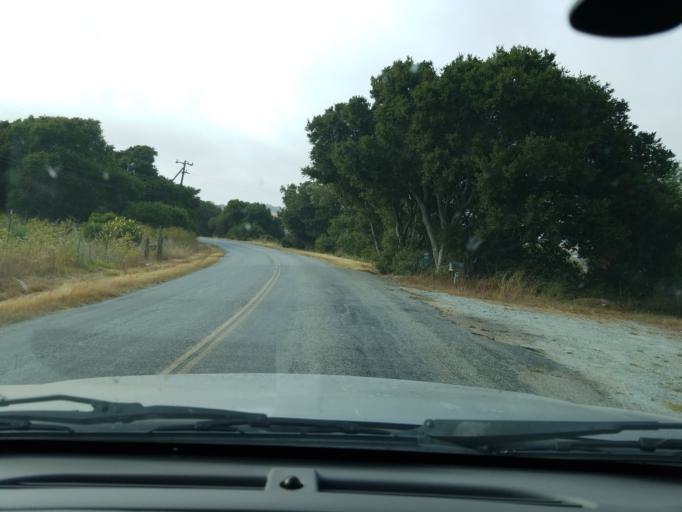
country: US
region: California
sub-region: Monterey County
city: Las Lomas
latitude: 36.8513
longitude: -121.7528
